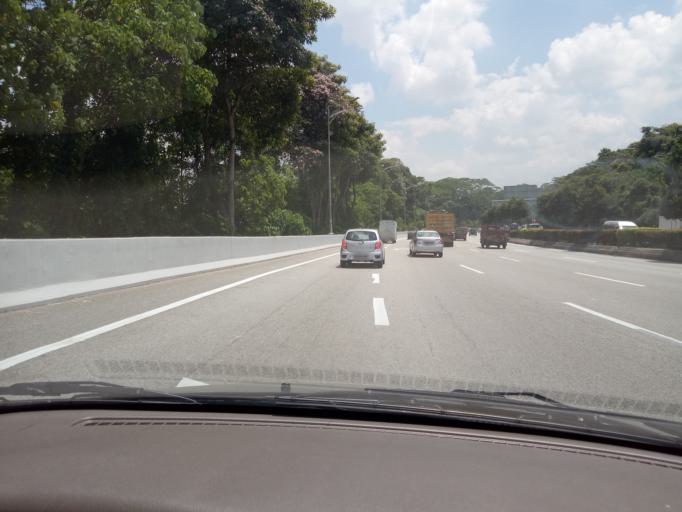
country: MY
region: Kuala Lumpur
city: Kuala Lumpur
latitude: 3.1239
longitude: 101.7034
